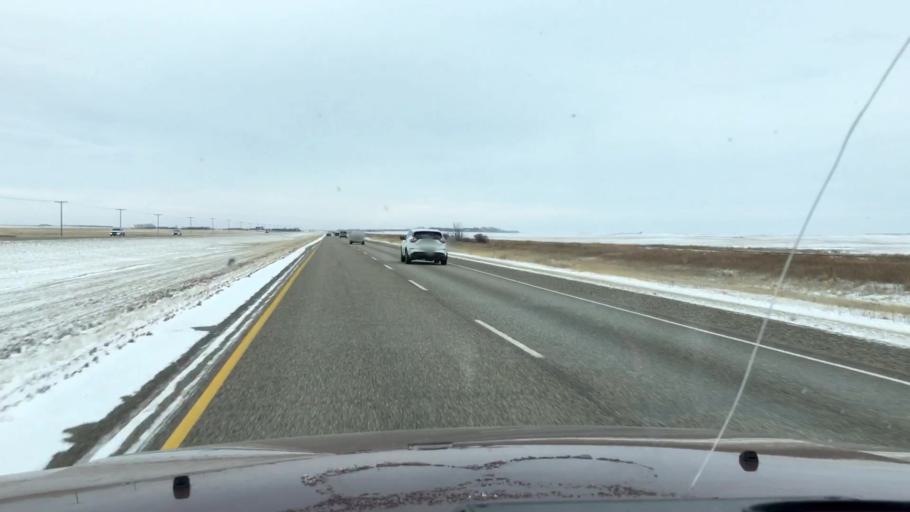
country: CA
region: Saskatchewan
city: Moose Jaw
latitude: 50.9955
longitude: -105.7585
